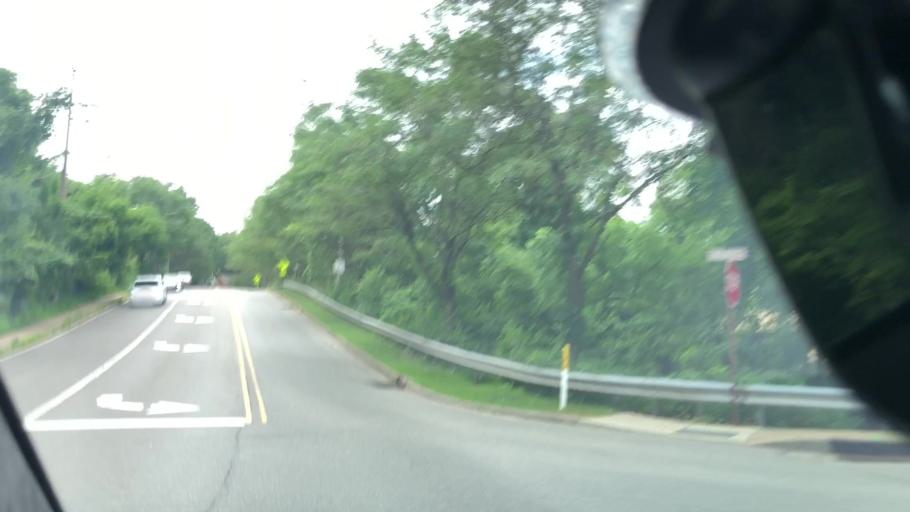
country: US
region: Pennsylvania
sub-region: Allegheny County
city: Mount Lebanon
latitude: 40.3676
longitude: -80.0614
